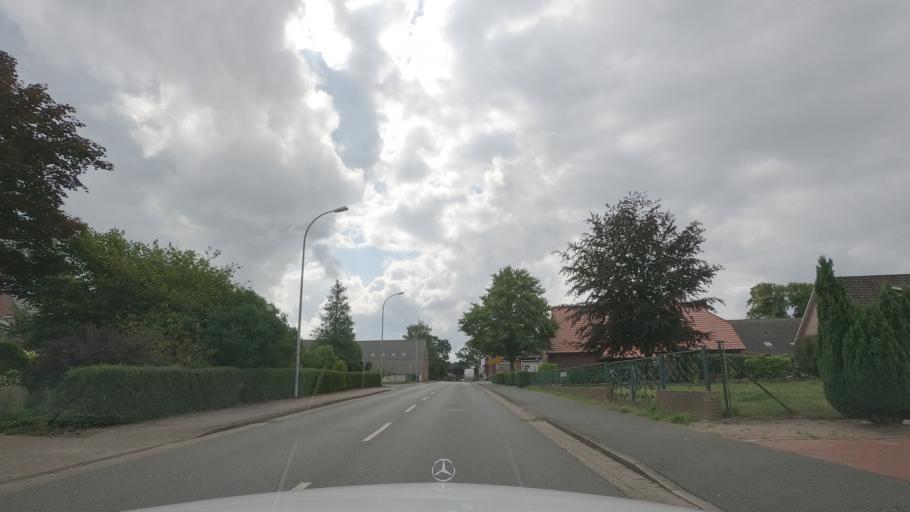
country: DE
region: Lower Saxony
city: Uthlede
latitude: 53.3098
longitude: 8.5790
